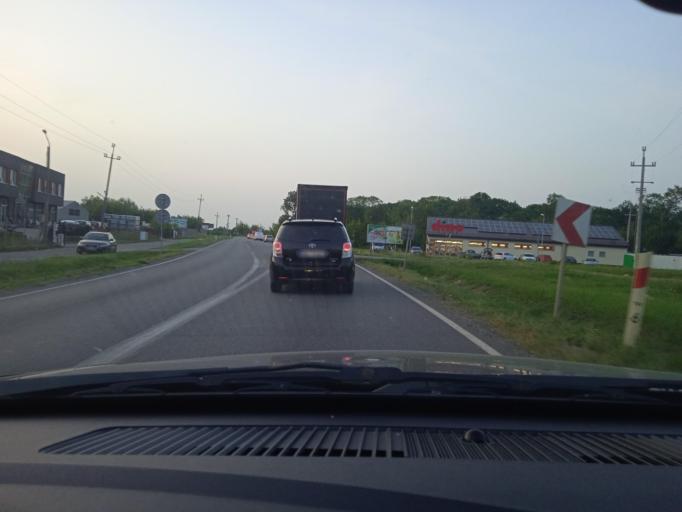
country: PL
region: Masovian Voivodeship
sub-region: Powiat nowodworski
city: Pomiechowek
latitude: 52.4666
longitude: 20.7224
